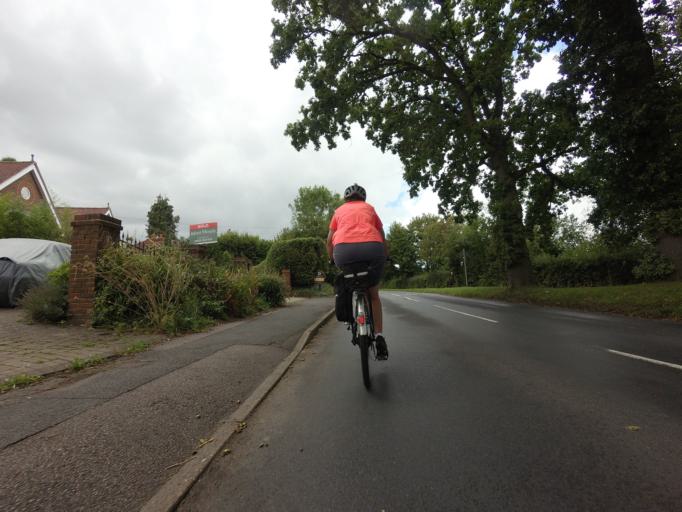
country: GB
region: England
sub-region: Kent
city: Shoreham
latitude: 51.3116
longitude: 0.1759
